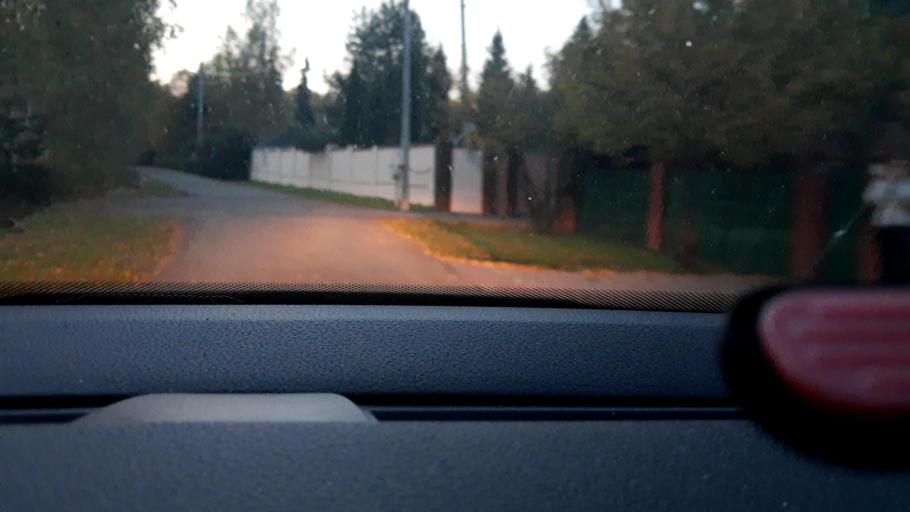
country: RU
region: Moskovskaya
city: Filimonki
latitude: 55.5354
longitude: 37.3596
